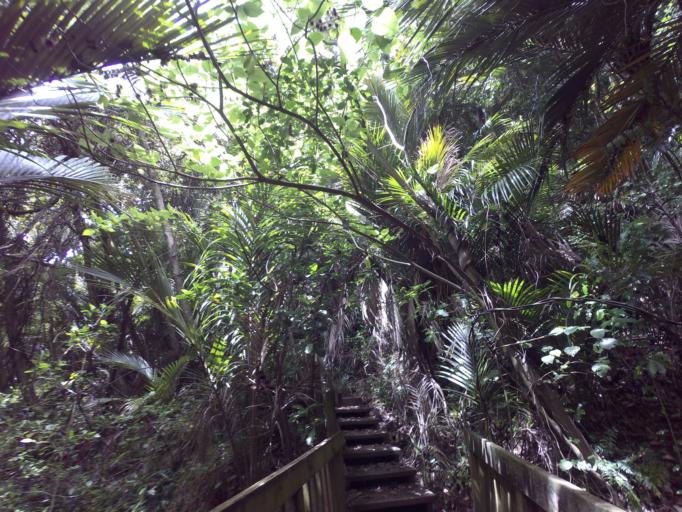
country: NZ
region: Auckland
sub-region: Auckland
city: Warkworth
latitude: -36.5359
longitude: 174.7127
